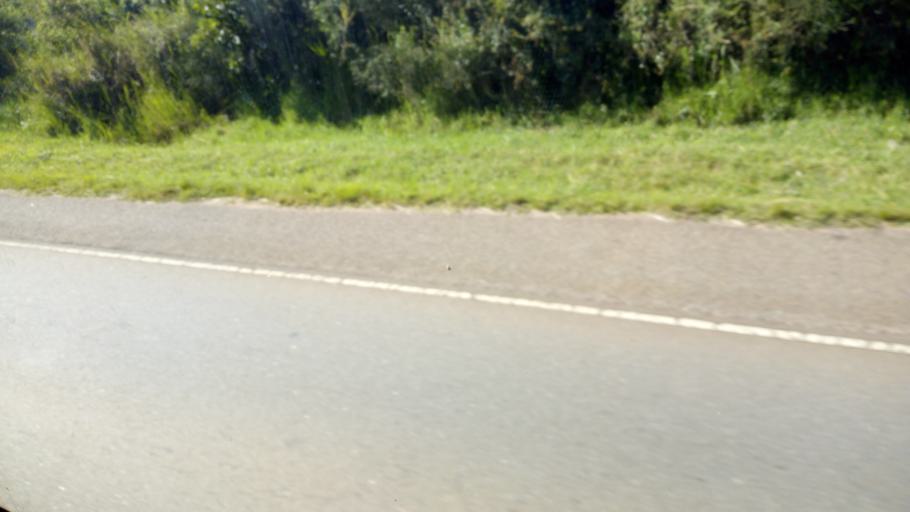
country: UG
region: Central Region
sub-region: Lyantonde District
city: Lyantonde
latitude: -0.4287
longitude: 31.1036
